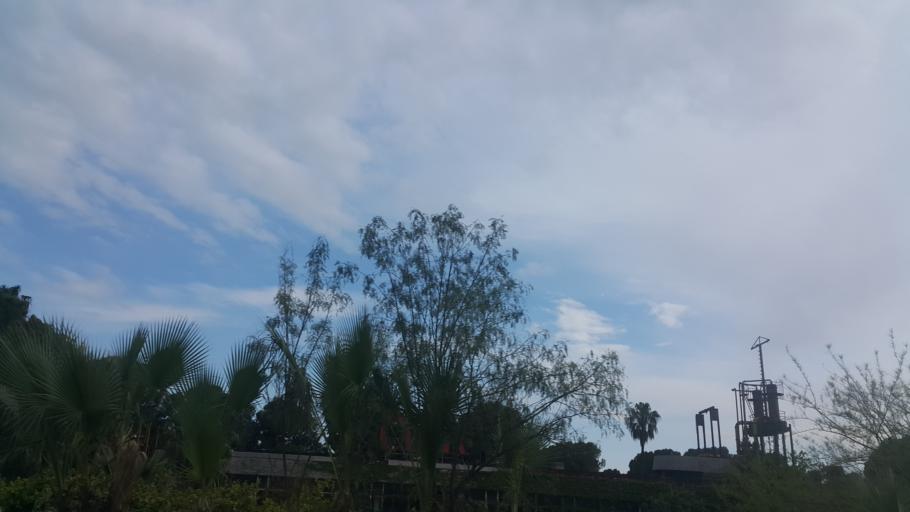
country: TR
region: Adana
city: Seyhan
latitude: 36.9965
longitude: 35.2348
